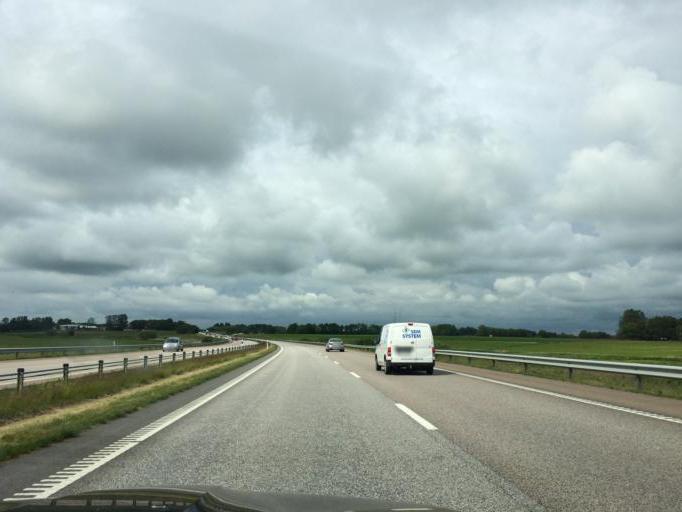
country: SE
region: Skane
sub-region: Angelholms Kommun
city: Strovelstorp
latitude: 56.1448
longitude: 12.8441
